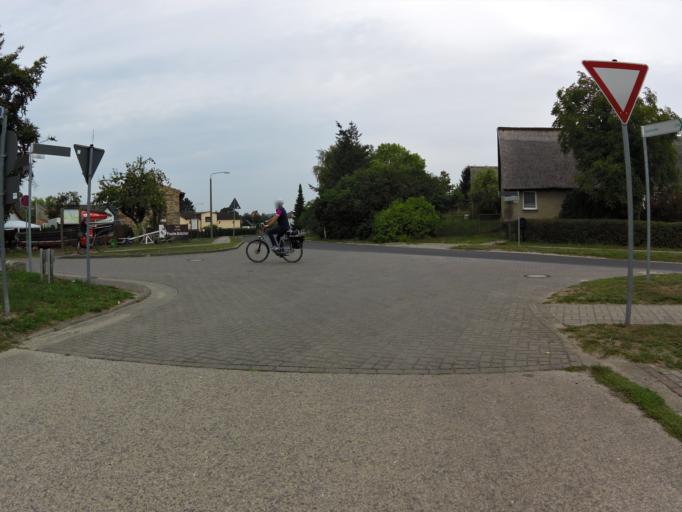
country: DE
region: Mecklenburg-Vorpommern
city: Seebad Heringsdorf
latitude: 53.8812
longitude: 14.1705
